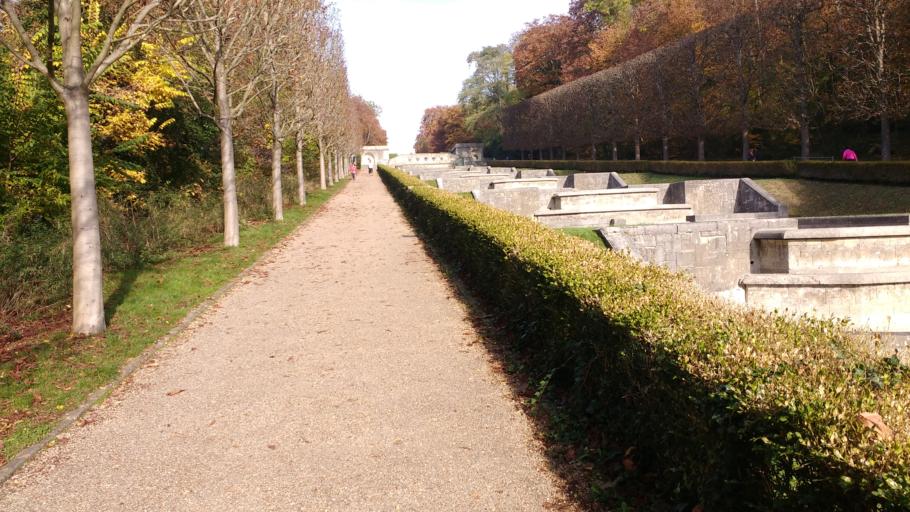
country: FR
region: Ile-de-France
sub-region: Departement des Hauts-de-Seine
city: Sceaux
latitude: 48.7697
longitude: 2.3014
